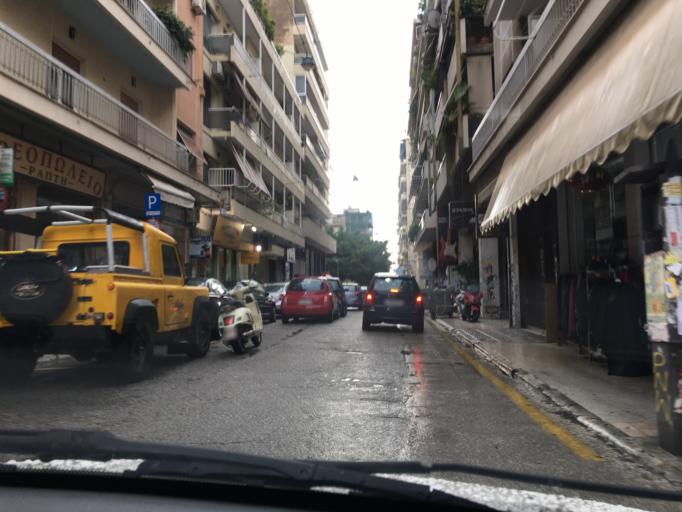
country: GR
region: West Greece
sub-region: Nomos Achaias
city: Patra
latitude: 38.2502
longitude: 21.7382
